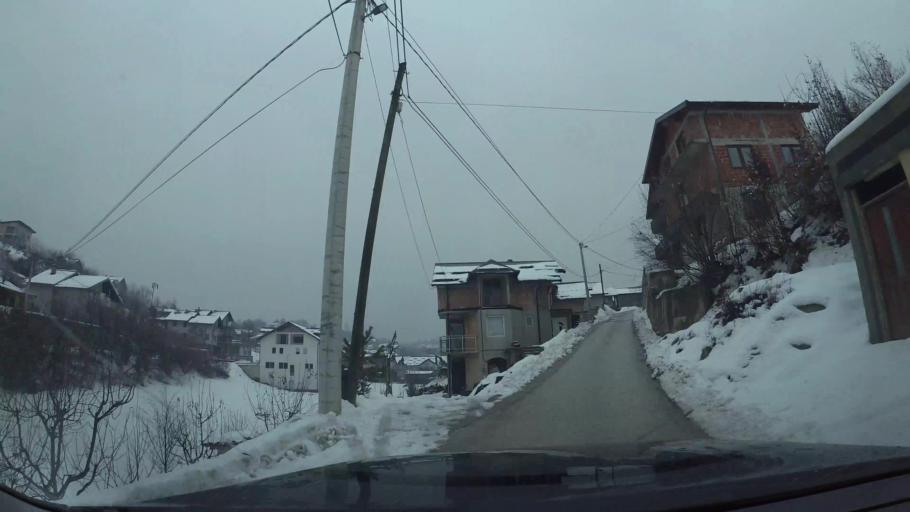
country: BA
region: Federation of Bosnia and Herzegovina
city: Hadzici
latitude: 43.8441
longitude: 18.2596
